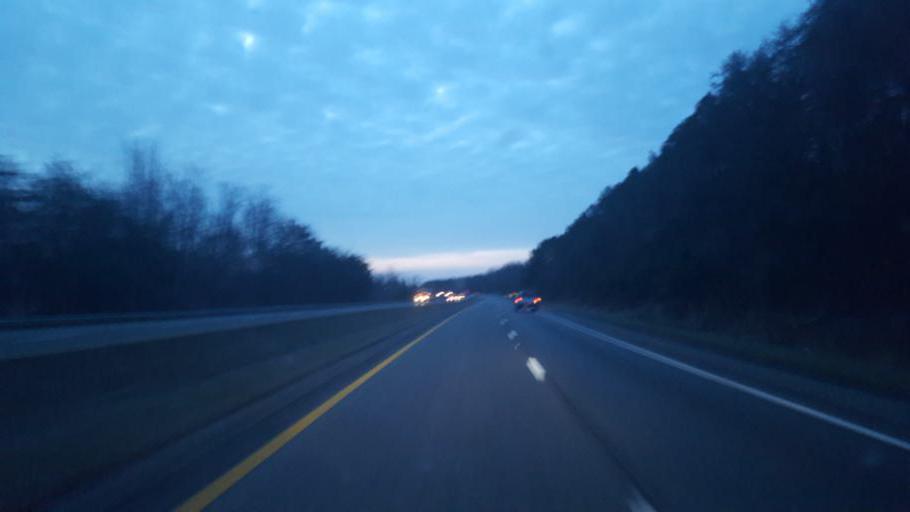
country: US
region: Ohio
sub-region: Jackson County
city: Jackson
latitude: 39.0189
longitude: -82.5774
